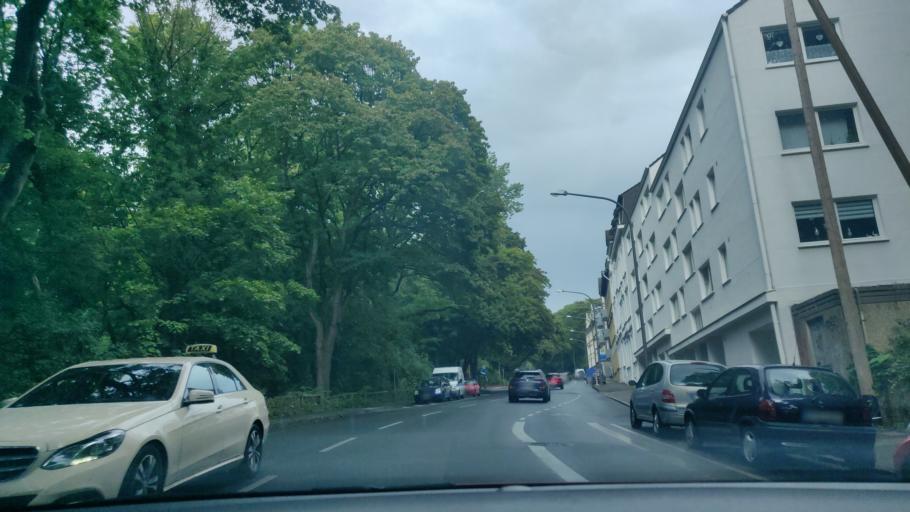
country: DE
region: North Rhine-Westphalia
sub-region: Regierungsbezirk Dusseldorf
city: Wuppertal
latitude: 51.2772
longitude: 7.1228
